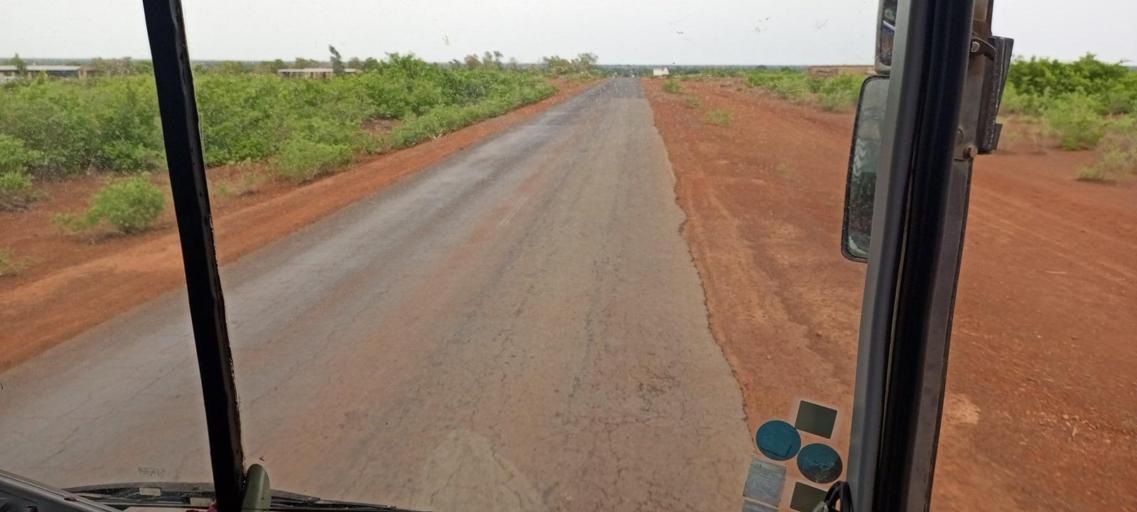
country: ML
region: Segou
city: Bla
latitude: 12.6988
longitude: -5.7240
